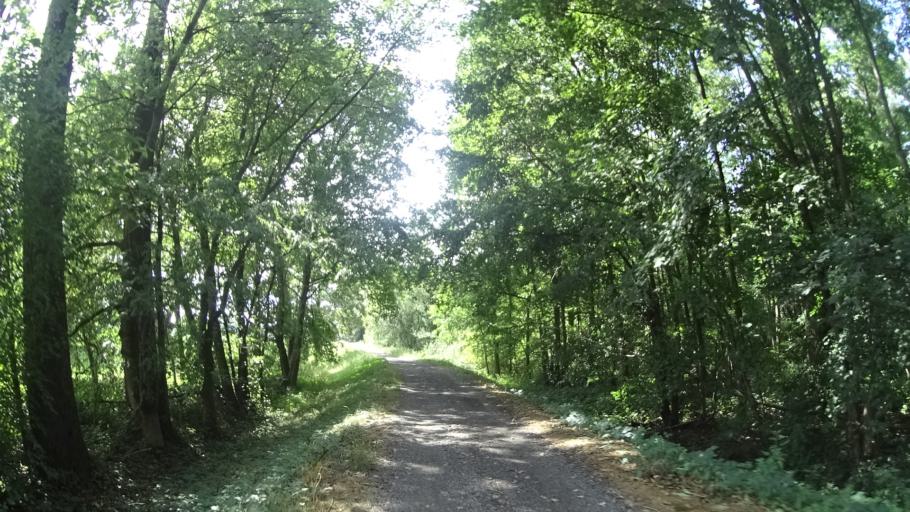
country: CZ
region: Olomoucky
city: Skrben
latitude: 49.6753
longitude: 17.1633
